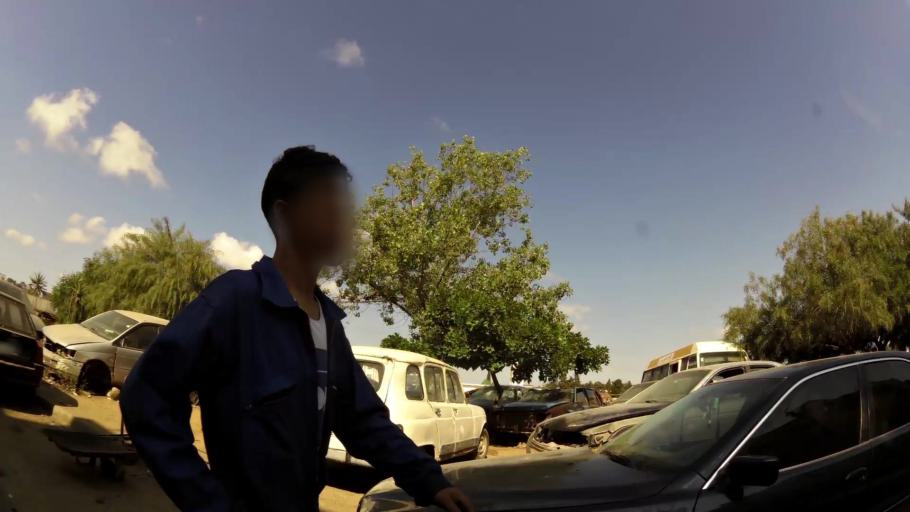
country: MA
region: Rabat-Sale-Zemmour-Zaer
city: Sale
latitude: 34.0454
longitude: -6.7771
